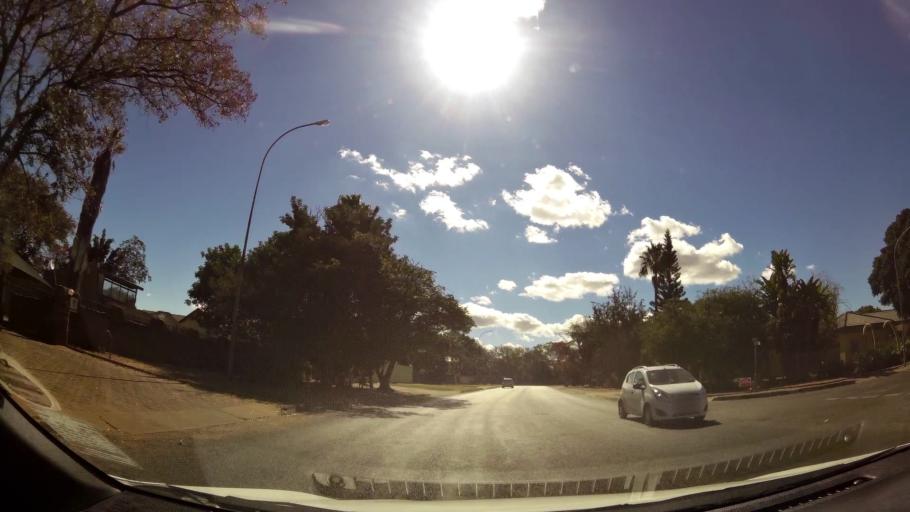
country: ZA
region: Limpopo
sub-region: Capricorn District Municipality
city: Polokwane
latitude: -23.9013
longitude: 29.4846
